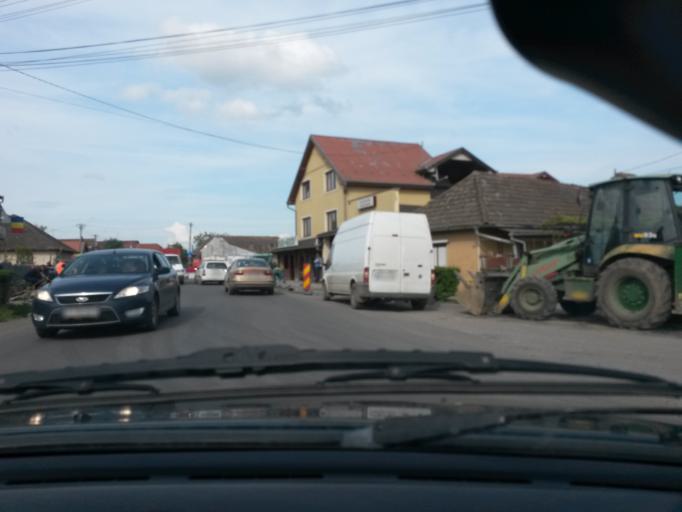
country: RO
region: Mures
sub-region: Comuna Sancraiu de Mures
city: Sancraiu de Mures
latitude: 46.5506
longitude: 24.5261
